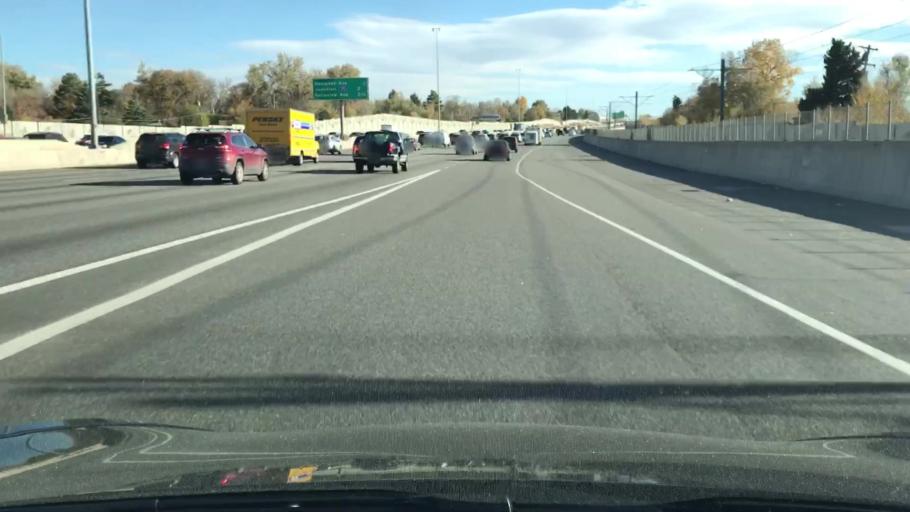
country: US
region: Colorado
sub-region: Arapahoe County
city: Glendale
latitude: 39.6656
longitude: -104.9249
